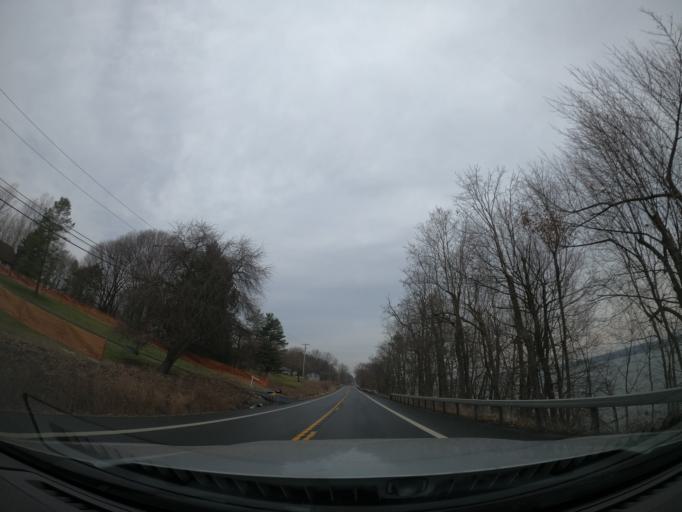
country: US
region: New York
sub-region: Cayuga County
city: Melrose Park
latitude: 42.8496
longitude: -76.5292
